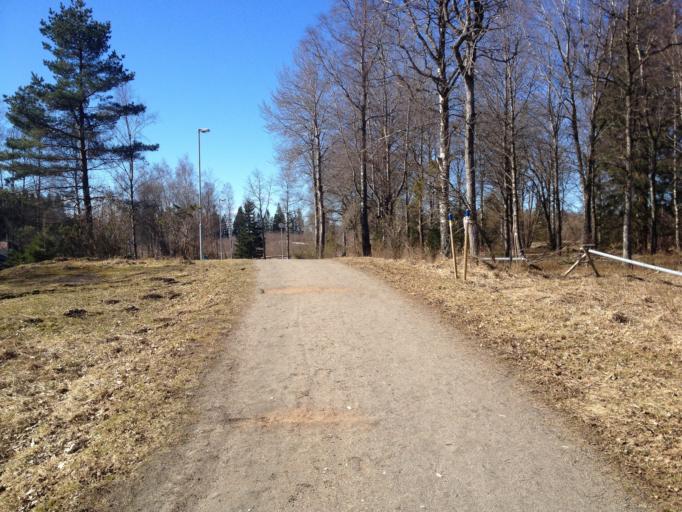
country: SE
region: Vaestra Goetaland
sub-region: Falkopings Kommun
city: Falkoeping
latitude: 58.1757
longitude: 13.5229
